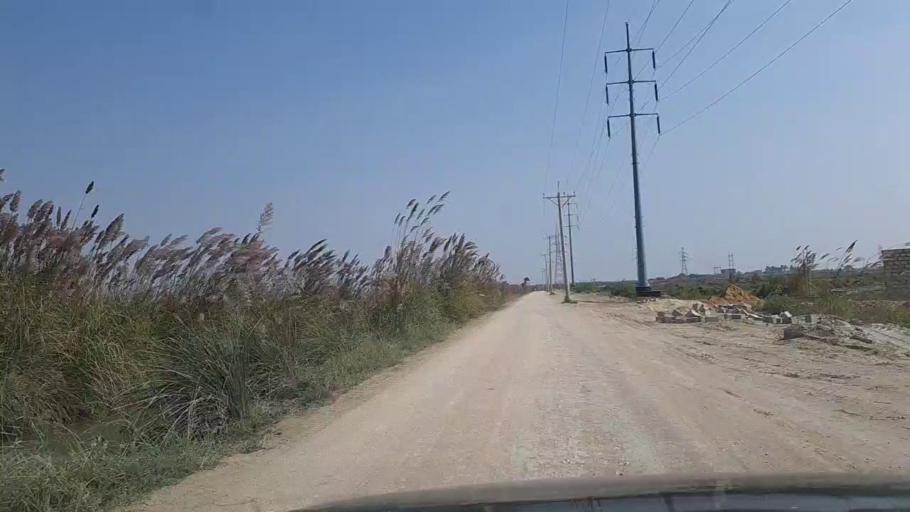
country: PK
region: Sindh
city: Gharo
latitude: 24.7219
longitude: 67.5491
